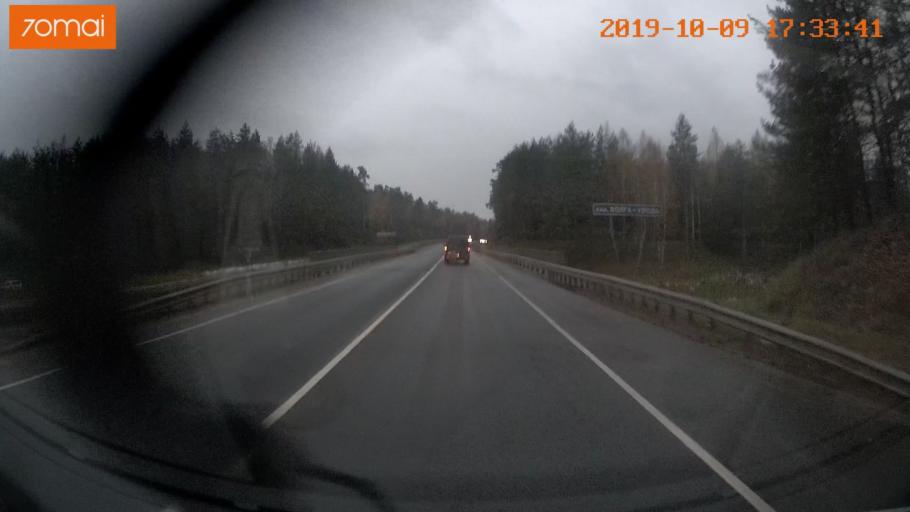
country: RU
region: Ivanovo
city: Bogorodskoye
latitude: 57.1148
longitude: 41.0181
